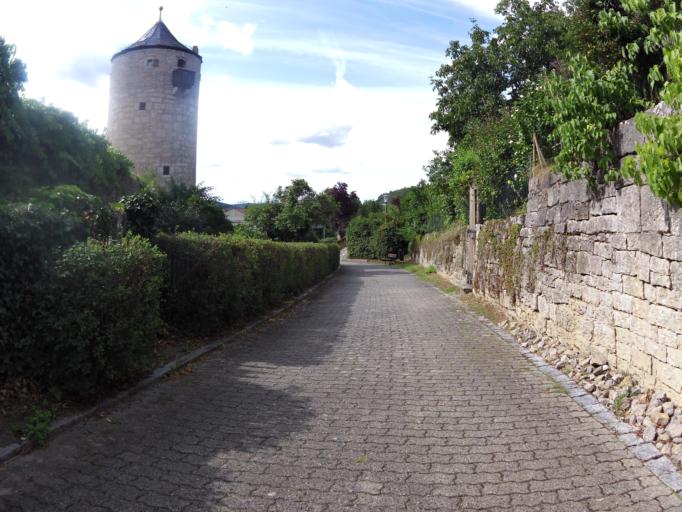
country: DE
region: Bavaria
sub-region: Regierungsbezirk Unterfranken
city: Sommerhausen
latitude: 49.7066
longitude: 10.0259
